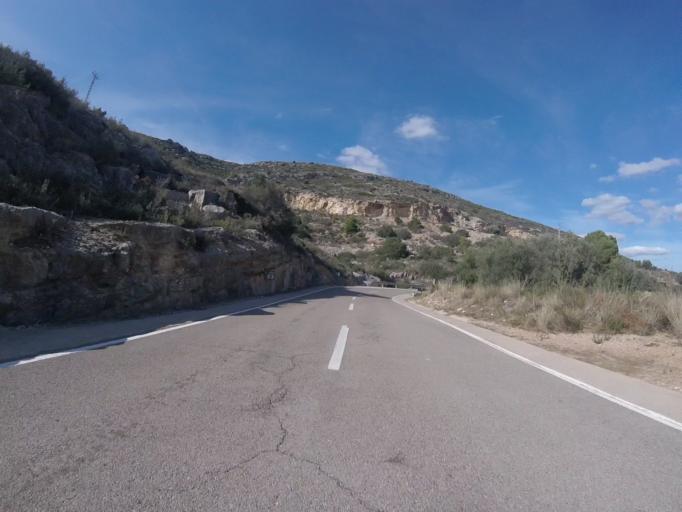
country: ES
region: Valencia
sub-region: Provincia de Castello
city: Alcala de Xivert
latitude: 40.2978
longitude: 0.1868
